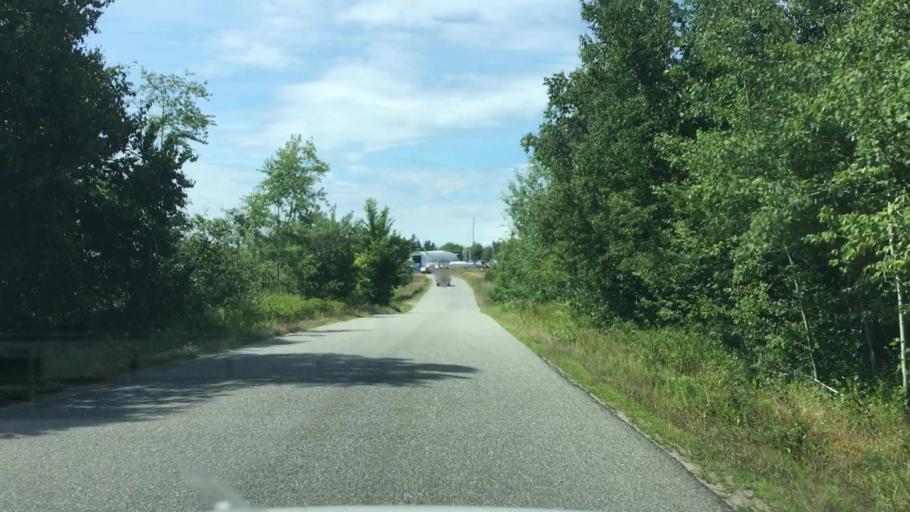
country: US
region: Maine
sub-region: Washington County
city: Eastport
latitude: 44.9064
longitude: -67.0084
